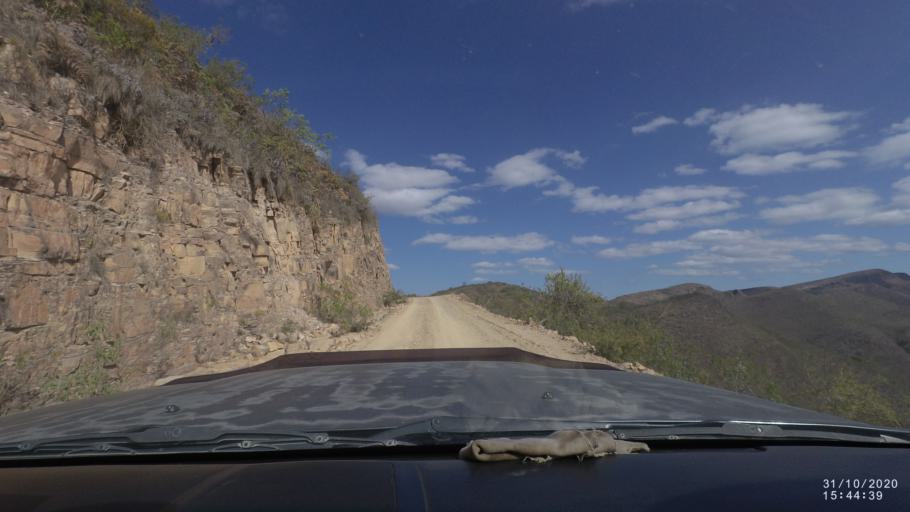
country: BO
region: Chuquisaca
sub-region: Provincia Zudanez
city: Mojocoya
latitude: -18.3177
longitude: -64.7222
